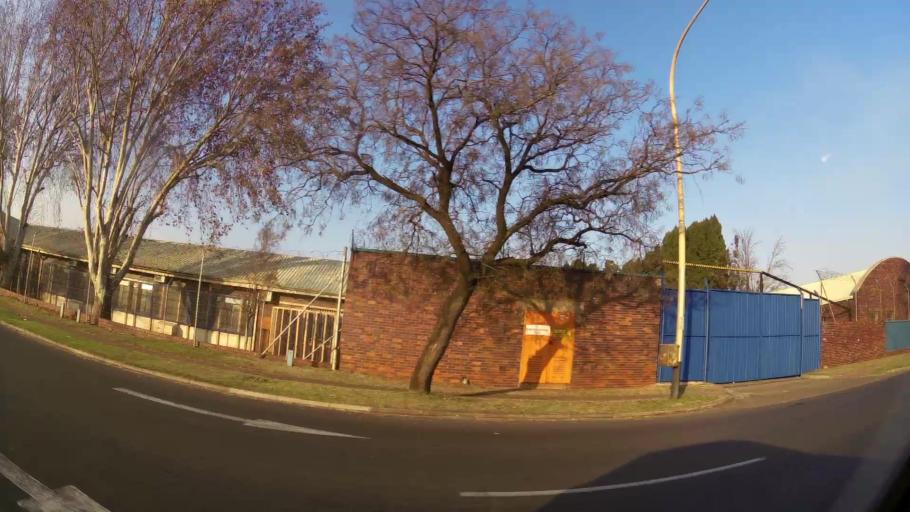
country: ZA
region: Gauteng
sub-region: Ekurhuleni Metropolitan Municipality
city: Springs
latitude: -26.2628
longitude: 28.4189
